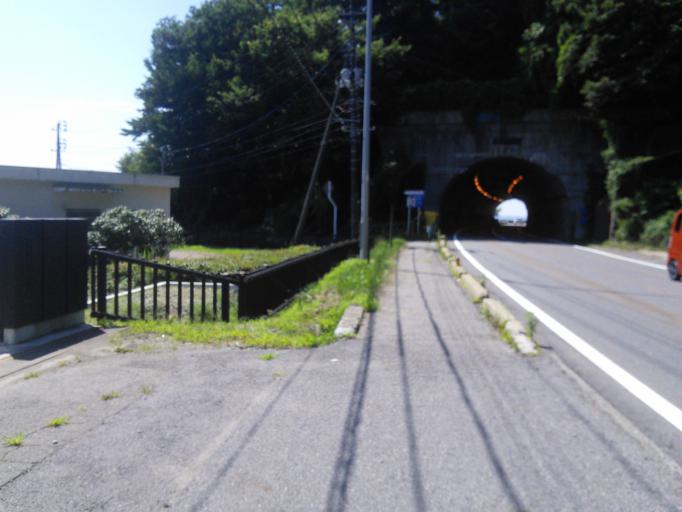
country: JP
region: Fukushima
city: Inawashiro
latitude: 37.4915
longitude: 140.1509
